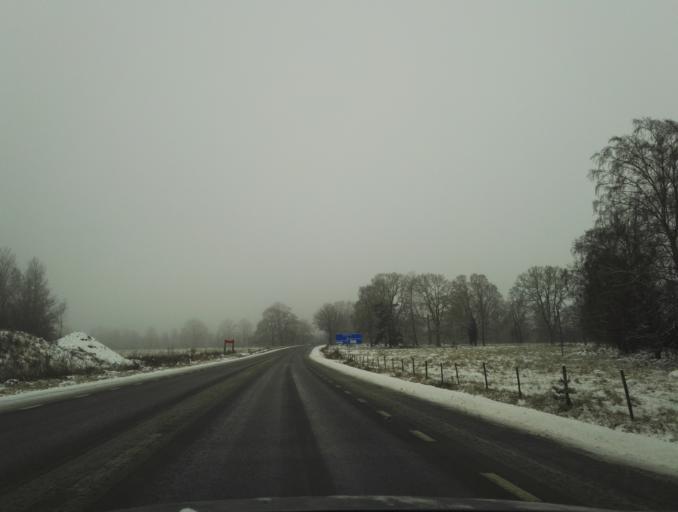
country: SE
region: Kronoberg
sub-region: Vaxjo Kommun
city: Vaexjoe
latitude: 56.8708
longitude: 14.7404
